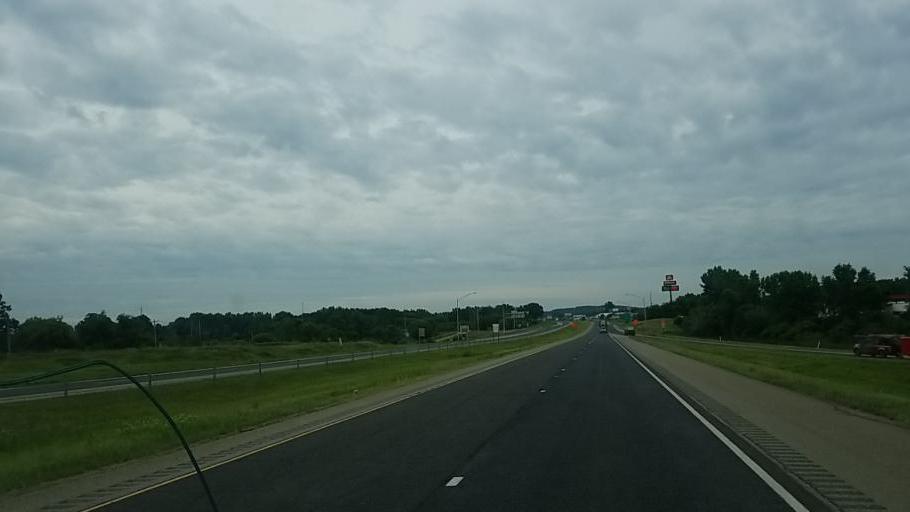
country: US
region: Indiana
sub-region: Steuben County
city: Fremont
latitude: 41.7462
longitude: -84.9969
